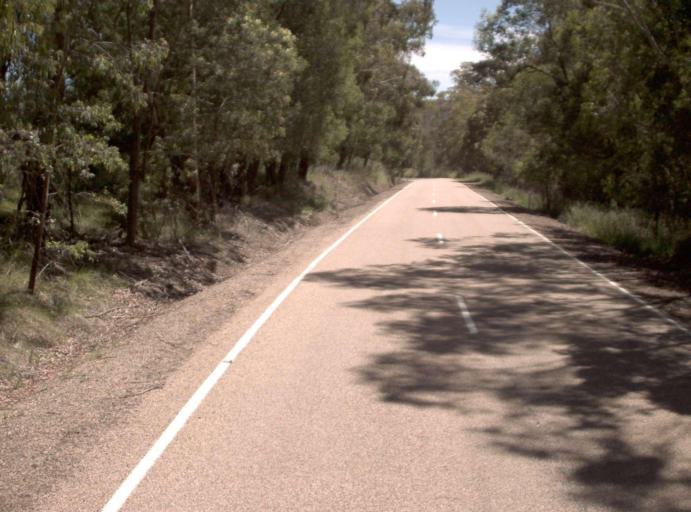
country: AU
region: Victoria
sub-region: East Gippsland
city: Lakes Entrance
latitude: -37.2449
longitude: 148.2553
